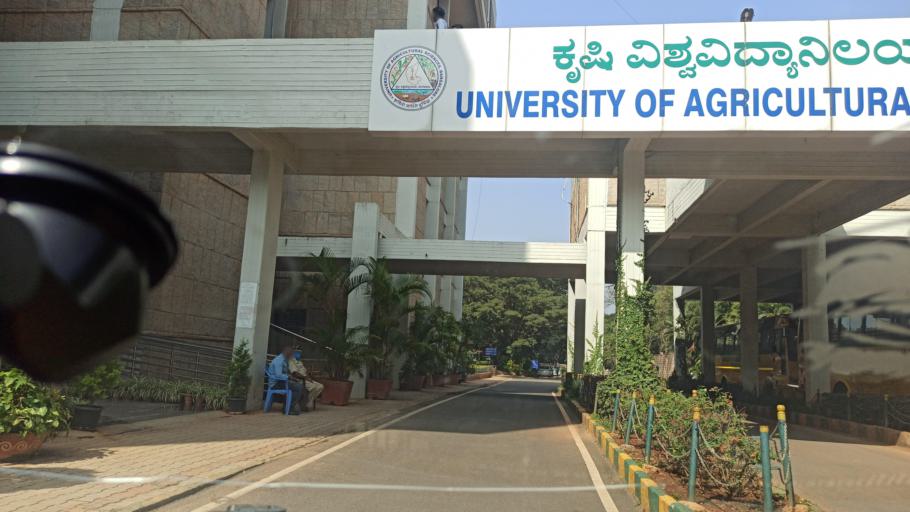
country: IN
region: Karnataka
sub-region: Bangalore Urban
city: Yelahanka
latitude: 13.0782
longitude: 77.5796
